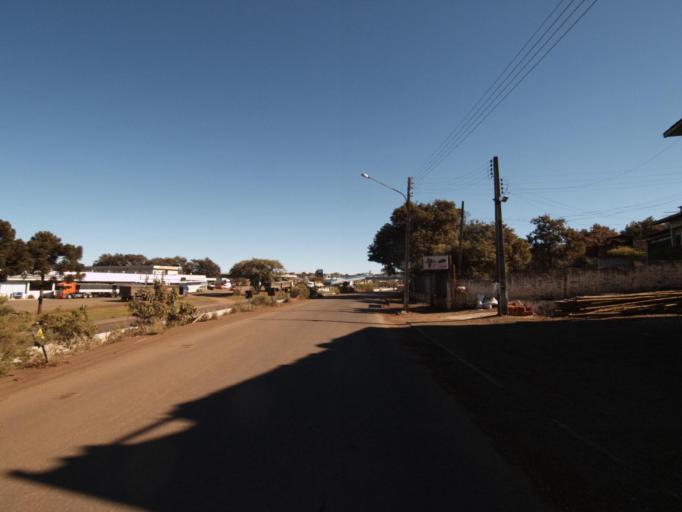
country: BR
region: Santa Catarina
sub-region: Xanxere
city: Xanxere
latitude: -26.8837
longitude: -52.4078
